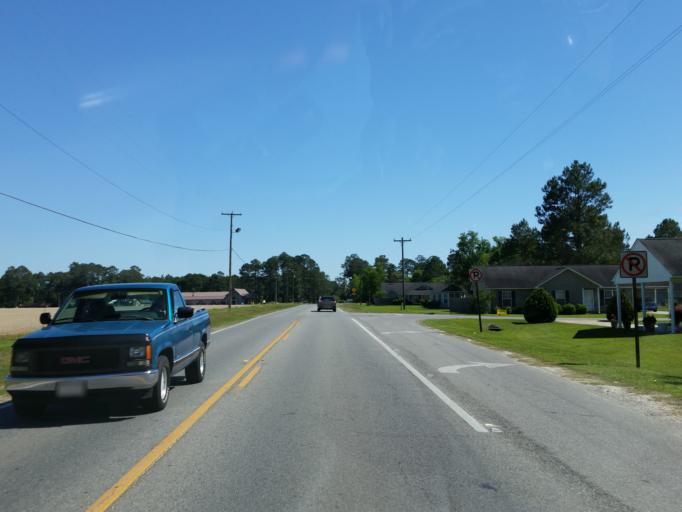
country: US
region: Georgia
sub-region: Cook County
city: Adel
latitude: 31.1183
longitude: -83.4152
